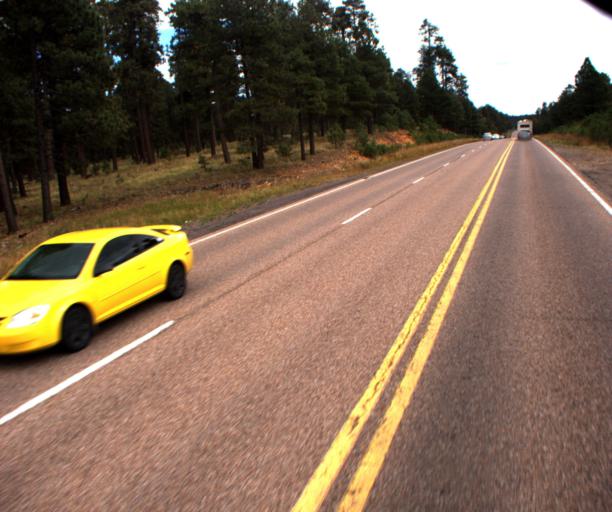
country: US
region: Arizona
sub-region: Navajo County
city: Heber-Overgaard
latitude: 34.3276
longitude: -110.8182
